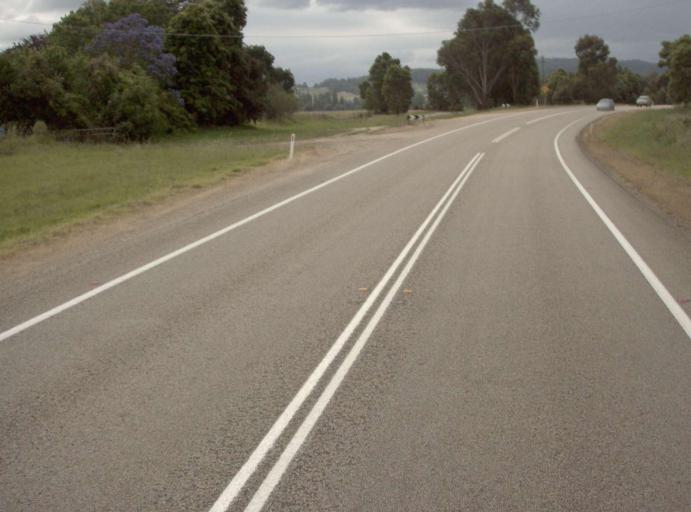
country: AU
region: Victoria
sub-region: East Gippsland
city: Lakes Entrance
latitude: -37.7162
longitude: 147.8381
